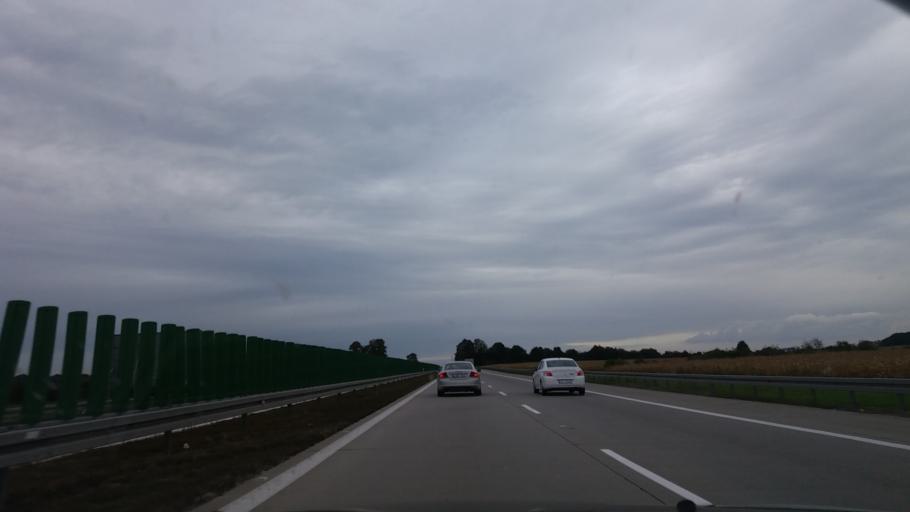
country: PL
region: Lower Silesian Voivodeship
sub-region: Powiat sredzki
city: Udanin
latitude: 51.0980
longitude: 16.4063
